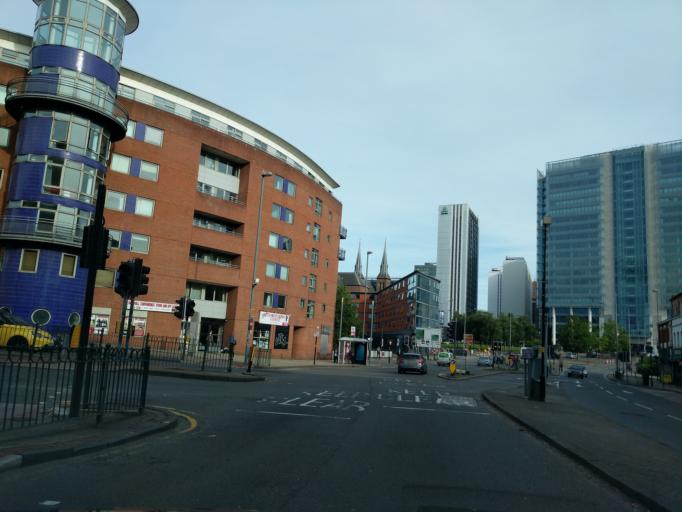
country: GB
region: England
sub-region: City and Borough of Birmingham
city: Birmingham
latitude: 52.4866
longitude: -1.9015
